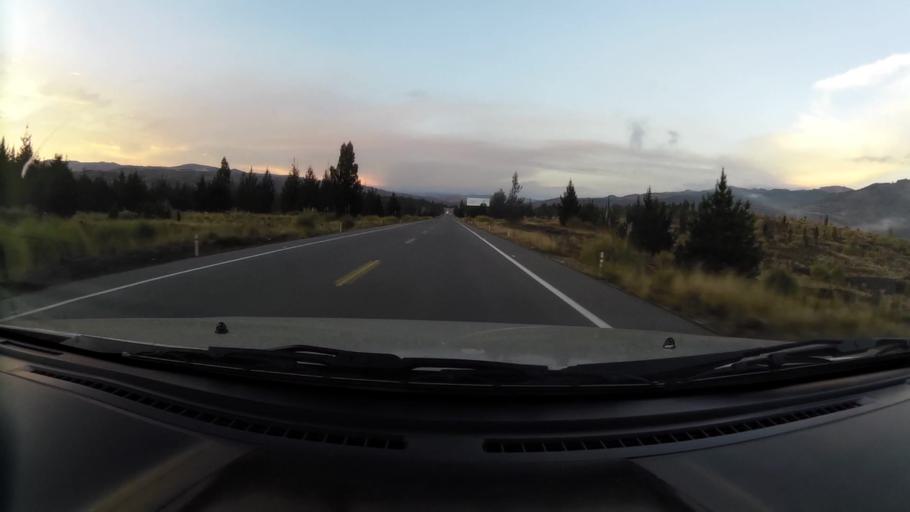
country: EC
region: Chimborazo
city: Alausi
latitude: -2.0366
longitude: -78.7366
